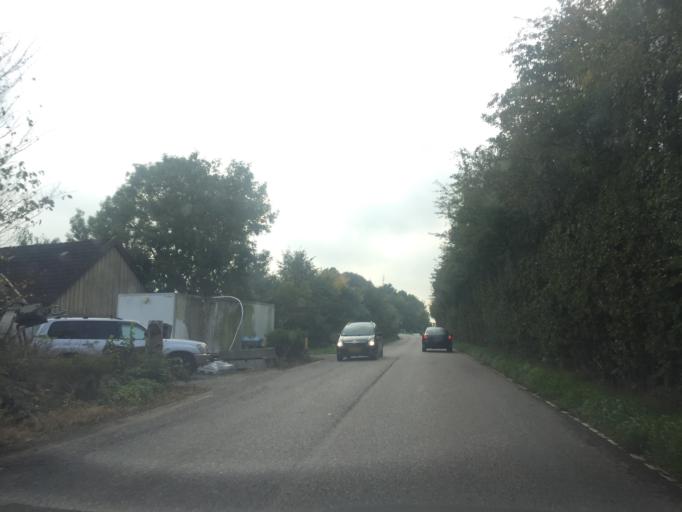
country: DK
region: Capital Region
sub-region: Hoje-Taastrup Kommune
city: Taastrup
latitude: 55.6669
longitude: 12.2815
